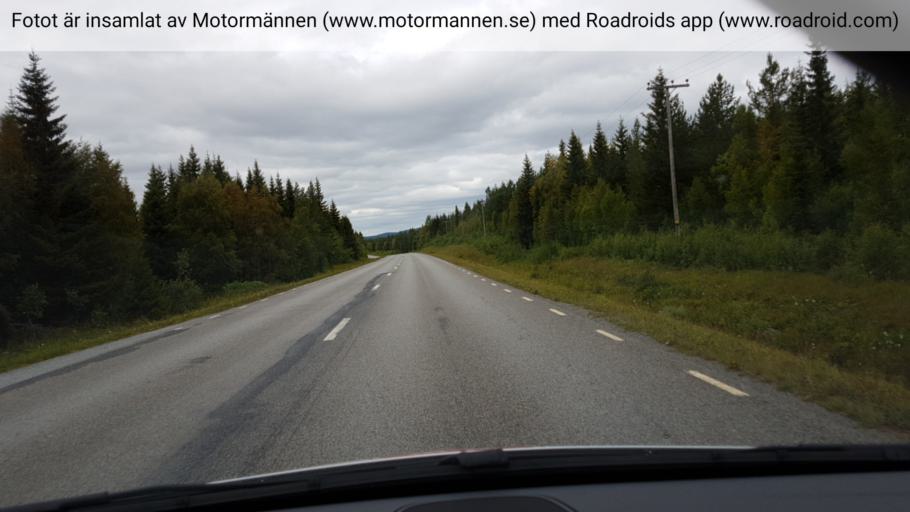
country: SE
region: Jaemtland
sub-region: Stroemsunds Kommun
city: Stroemsund
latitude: 64.2731
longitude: 15.3801
